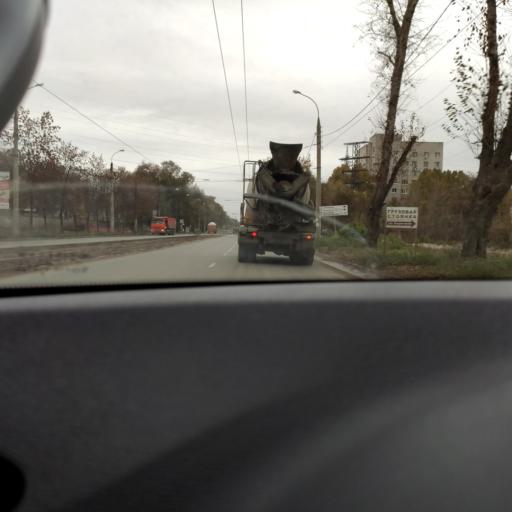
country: RU
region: Samara
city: Smyshlyayevka
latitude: 53.1986
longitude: 50.2874
